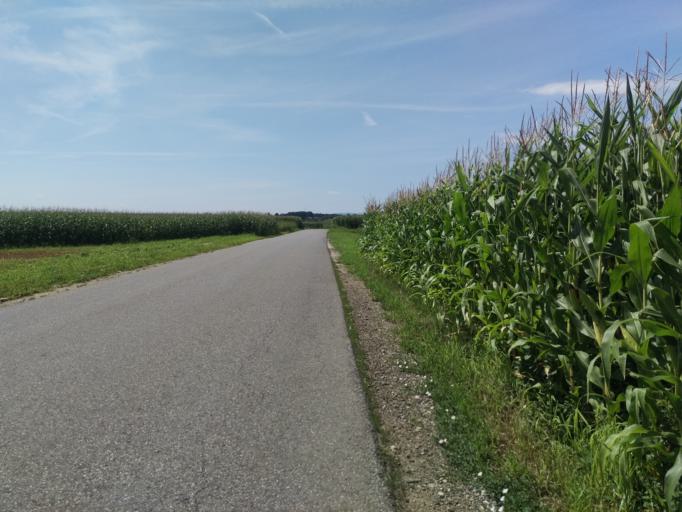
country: AT
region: Styria
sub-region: Politischer Bezirk Graz-Umgebung
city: Unterpremstatten
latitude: 46.9832
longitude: 15.4123
